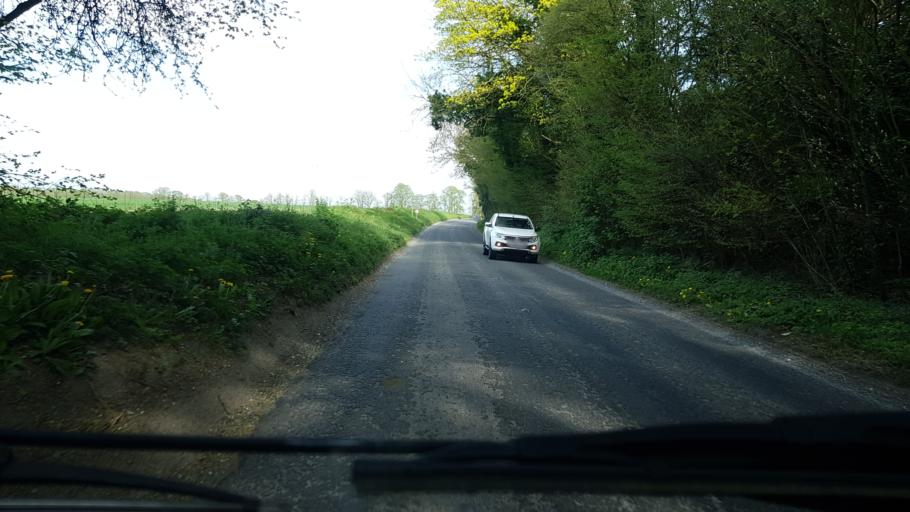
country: GB
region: England
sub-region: Hampshire
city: Overton
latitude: 51.2555
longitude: -1.1899
